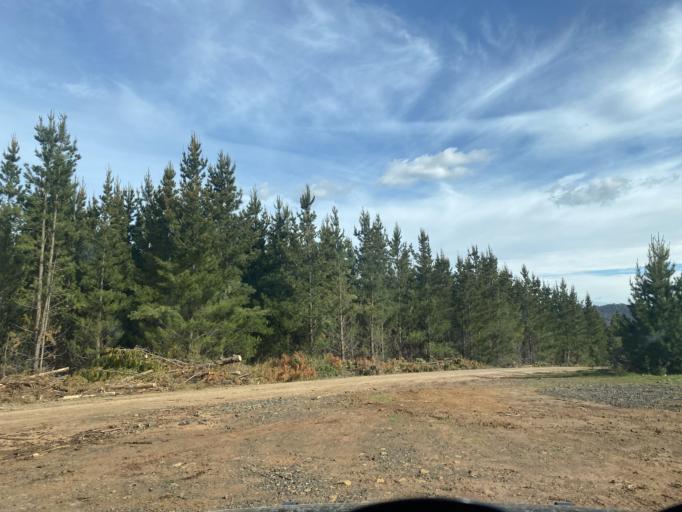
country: AU
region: Victoria
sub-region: Mansfield
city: Mansfield
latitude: -36.8335
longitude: 146.1793
